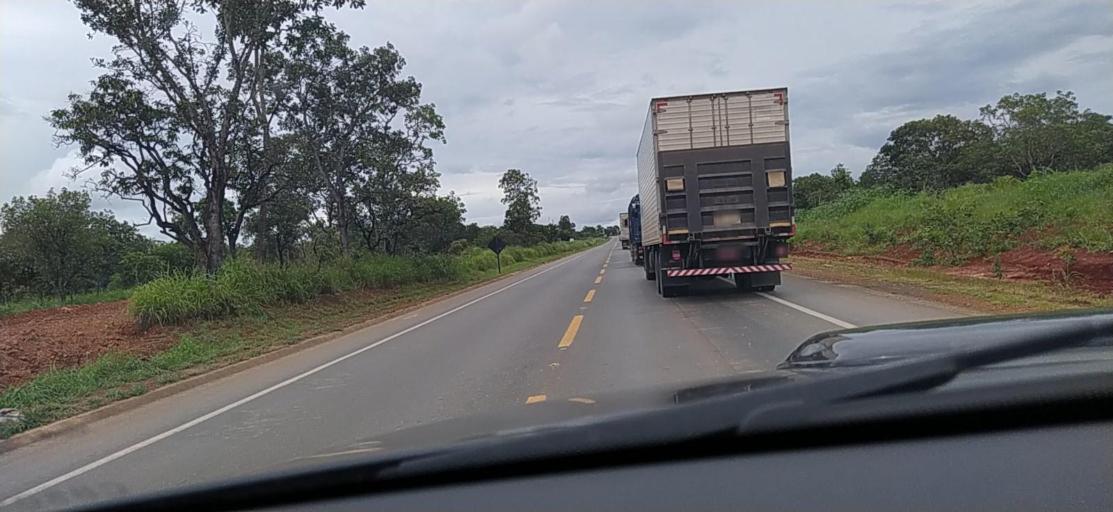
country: BR
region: Minas Gerais
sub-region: Curvelo
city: Curvelo
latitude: -18.7203
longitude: -44.4421
